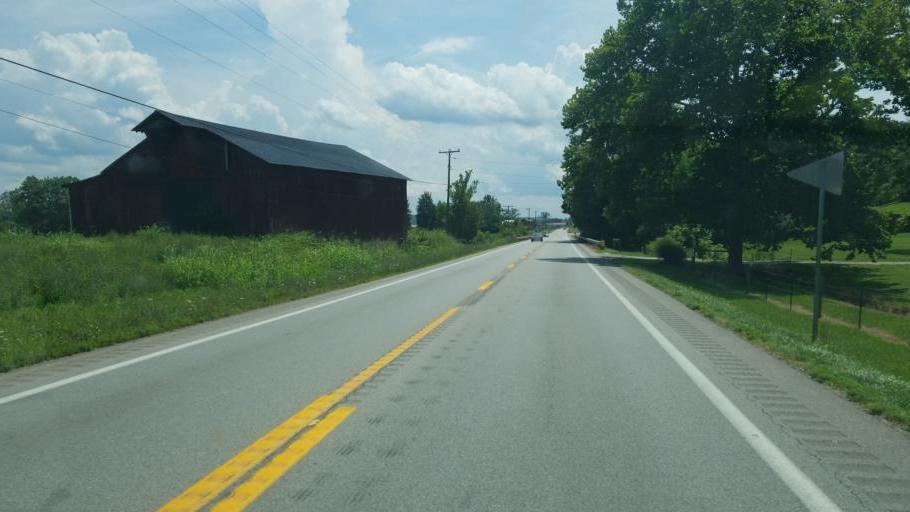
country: US
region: West Virginia
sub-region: Putnam County
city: Buffalo
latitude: 38.7198
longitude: -81.9698
